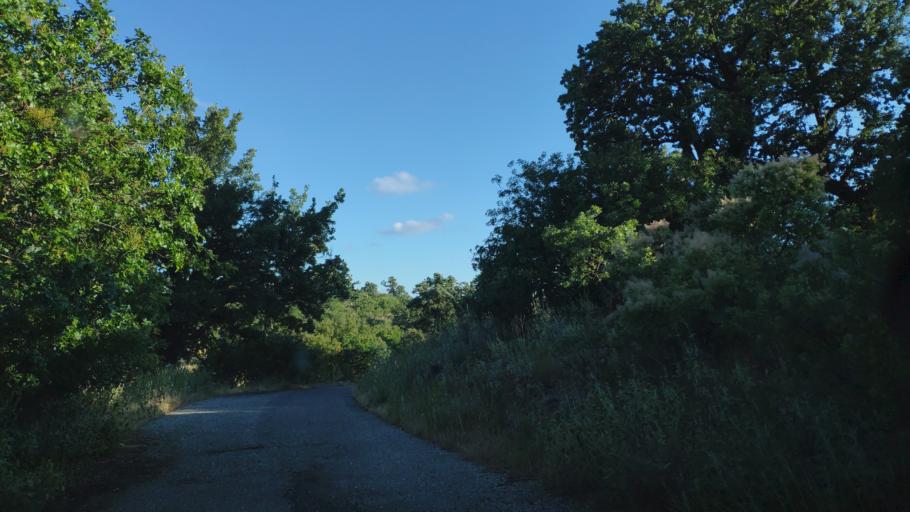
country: GR
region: West Greece
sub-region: Nomos Aitolias kai Akarnanias
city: Fitiai
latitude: 38.6362
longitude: 21.1966
